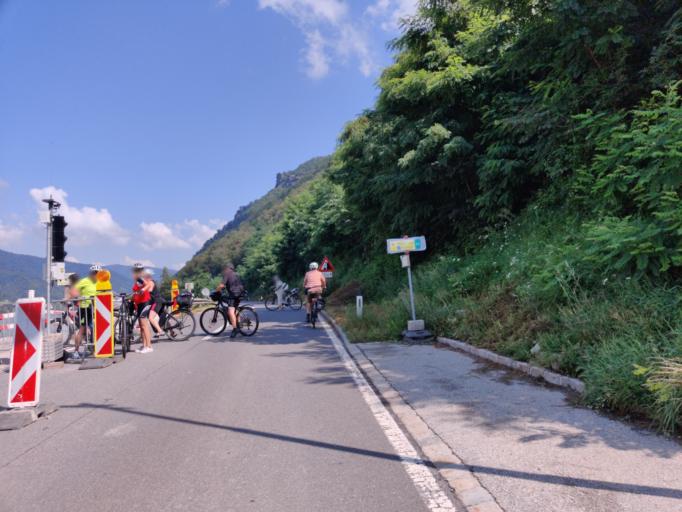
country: AT
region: Lower Austria
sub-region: Politischer Bezirk Krems
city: Aggsbach
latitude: 48.3173
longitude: 15.4138
